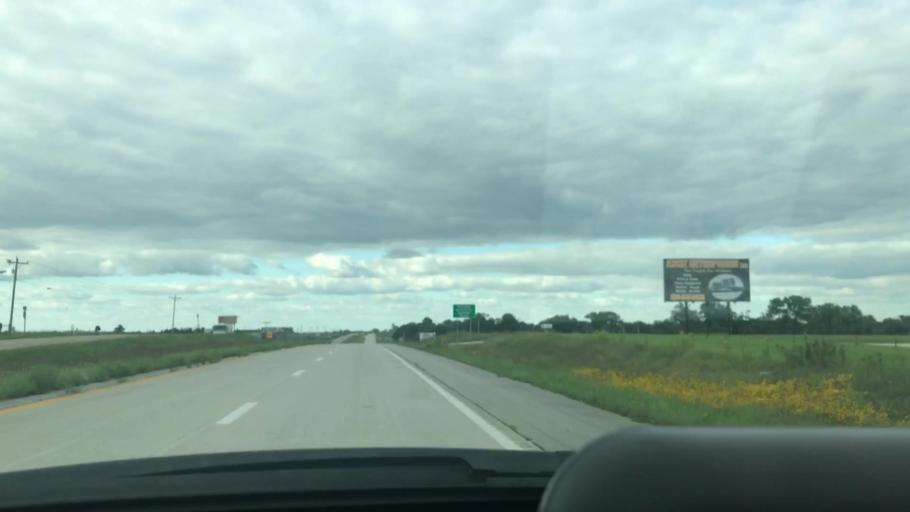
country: US
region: Missouri
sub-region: Benton County
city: Lincoln
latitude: 38.3444
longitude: -93.3401
